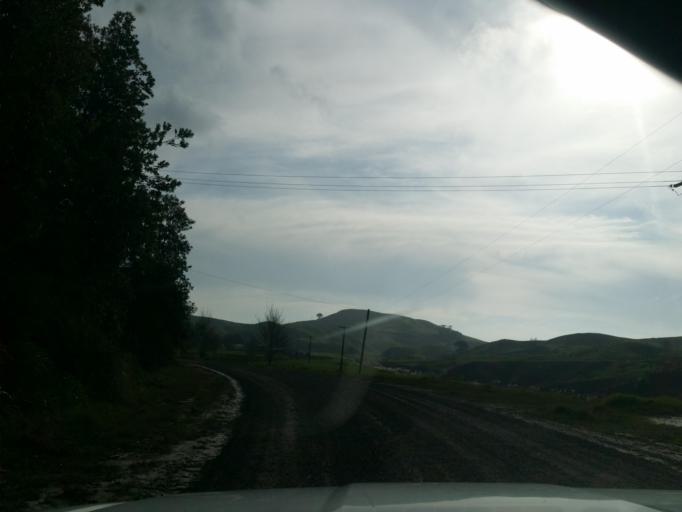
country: NZ
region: Northland
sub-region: Kaipara District
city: Dargaville
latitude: -35.8646
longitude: 173.7266
